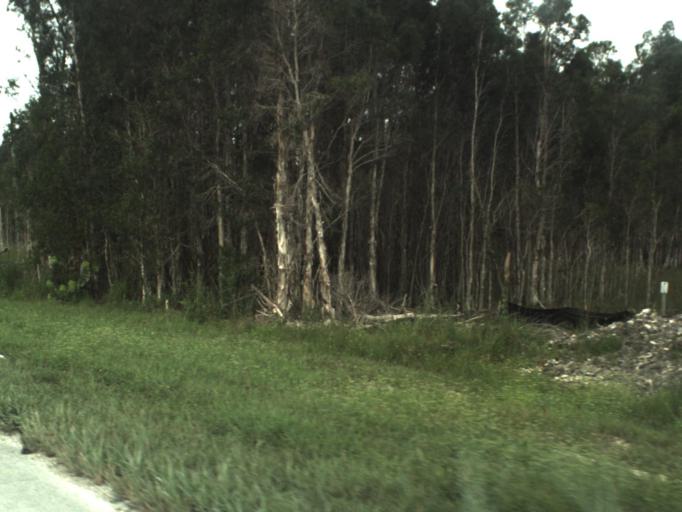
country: US
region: Florida
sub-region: Miami-Dade County
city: Kendall West
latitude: 25.7560
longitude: -80.4812
